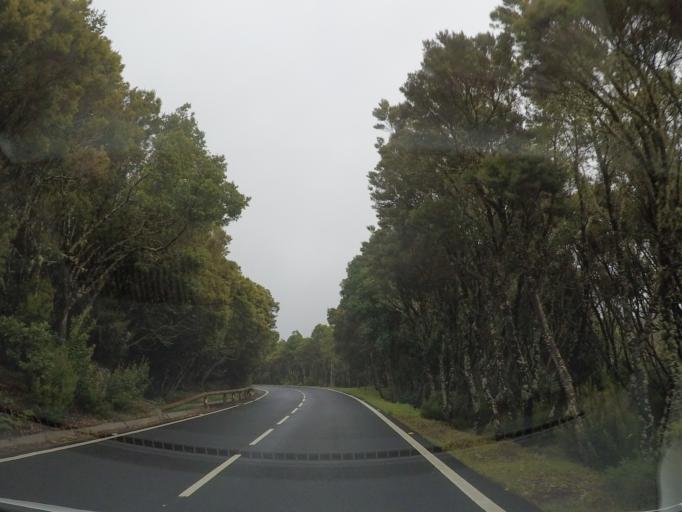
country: ES
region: Canary Islands
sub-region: Provincia de Santa Cruz de Tenerife
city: Vallehermosa
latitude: 28.1273
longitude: -17.2665
